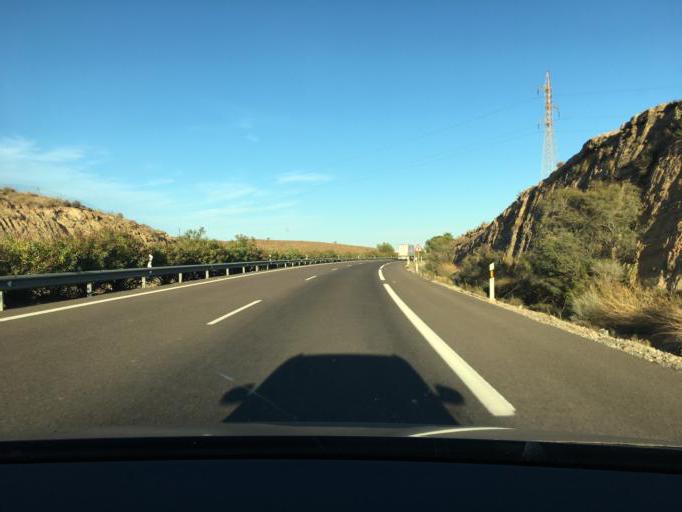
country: ES
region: Andalusia
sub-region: Provincia de Almeria
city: Bedar
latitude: 37.1475
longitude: -1.9839
